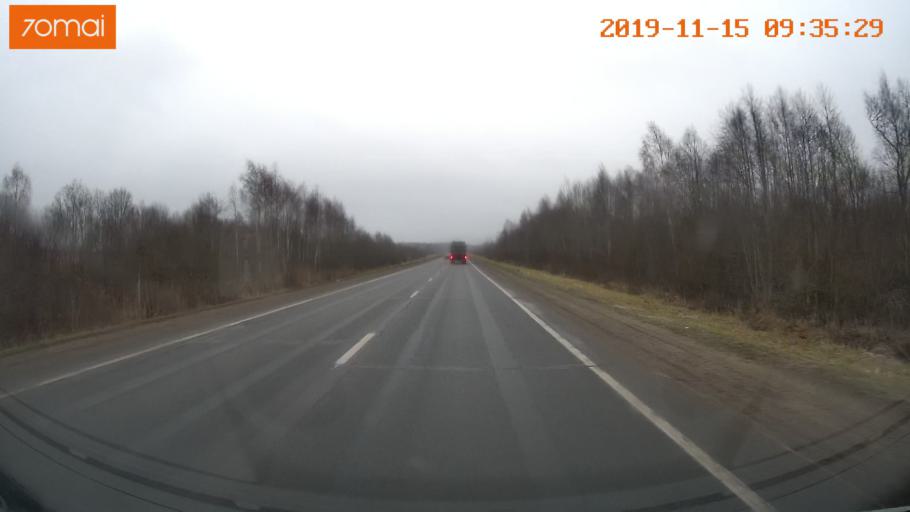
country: RU
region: Vologda
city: Sheksna
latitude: 59.2541
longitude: 38.4001
